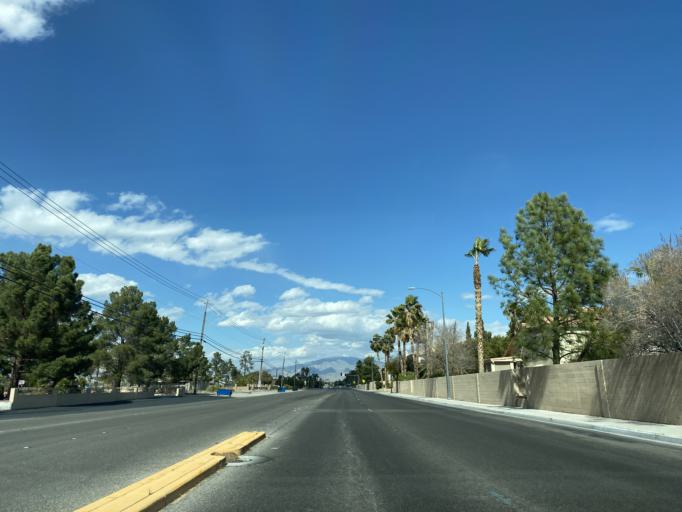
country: US
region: Nevada
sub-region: Clark County
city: Spring Valley
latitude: 36.2412
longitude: -115.2604
